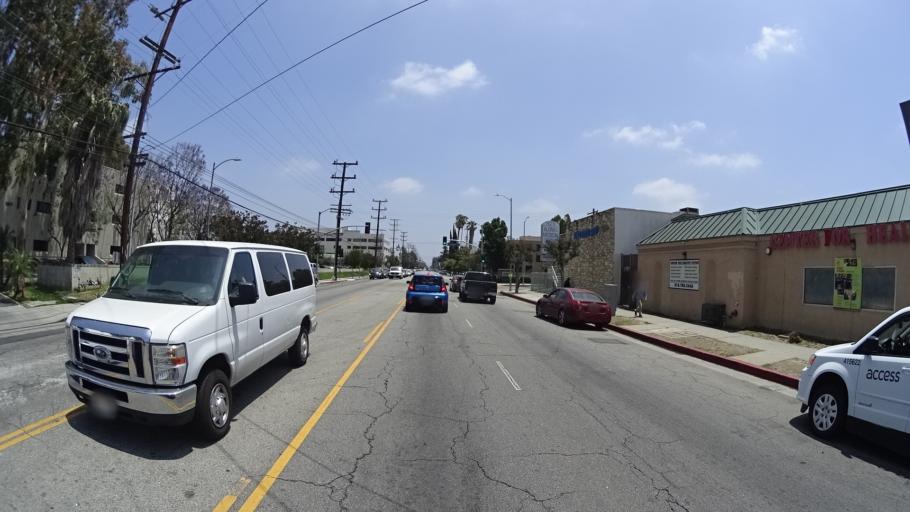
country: US
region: California
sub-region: Los Angeles County
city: Van Nuys
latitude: 34.1939
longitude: -118.4647
